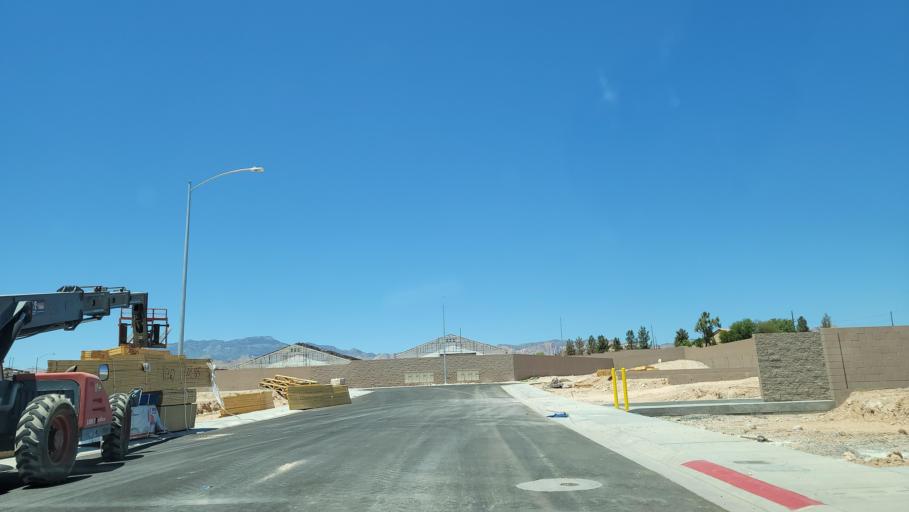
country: US
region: Nevada
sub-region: Clark County
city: Enterprise
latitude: 36.0251
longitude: -115.3033
